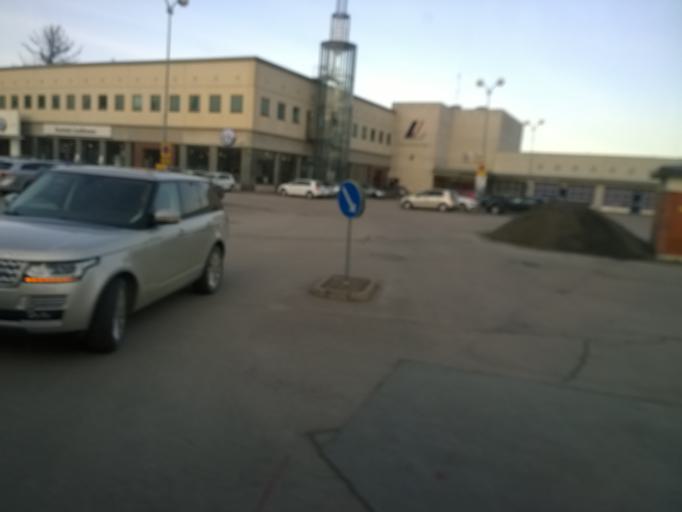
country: FI
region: Pirkanmaa
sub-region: Tampere
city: Tampere
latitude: 61.4828
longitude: 23.7632
